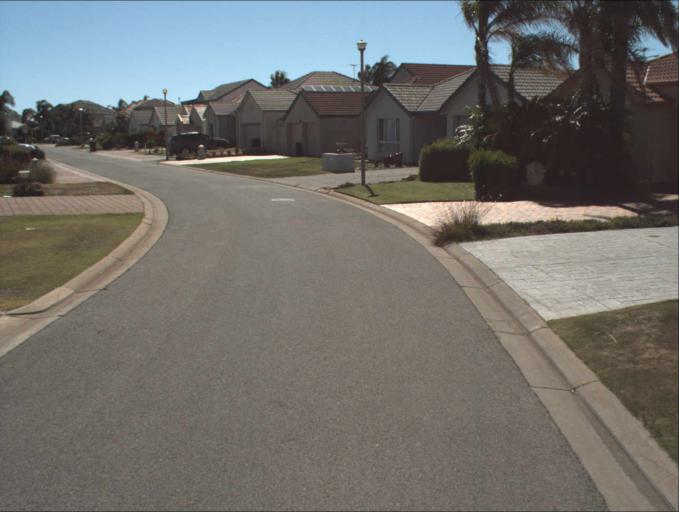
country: AU
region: South Australia
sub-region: Port Adelaide Enfield
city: Birkenhead
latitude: -34.7959
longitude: 138.4901
